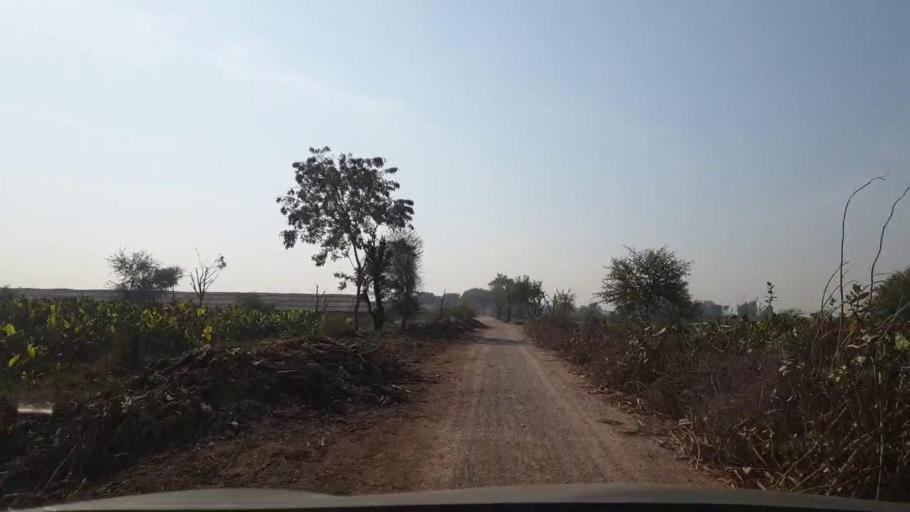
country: PK
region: Sindh
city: Tando Allahyar
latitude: 25.5929
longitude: 68.7382
